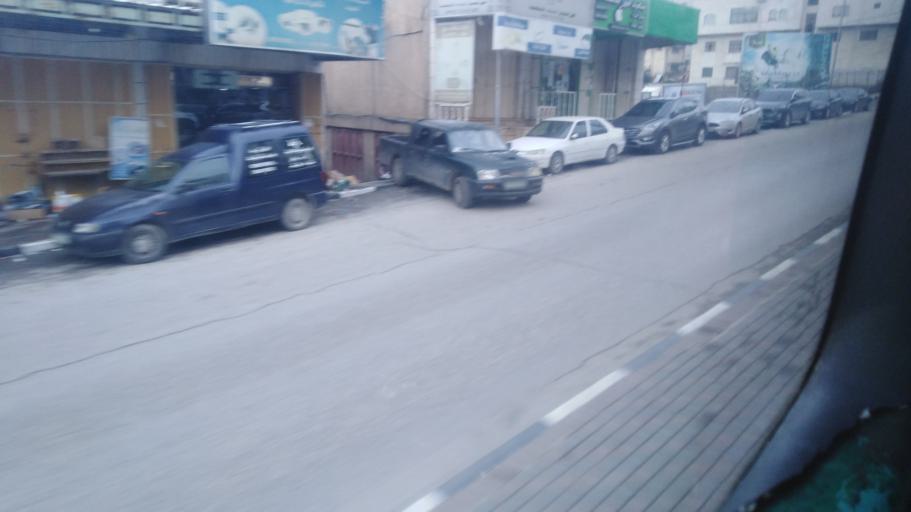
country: PS
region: West Bank
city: Hebron
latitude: 31.5288
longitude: 35.0890
